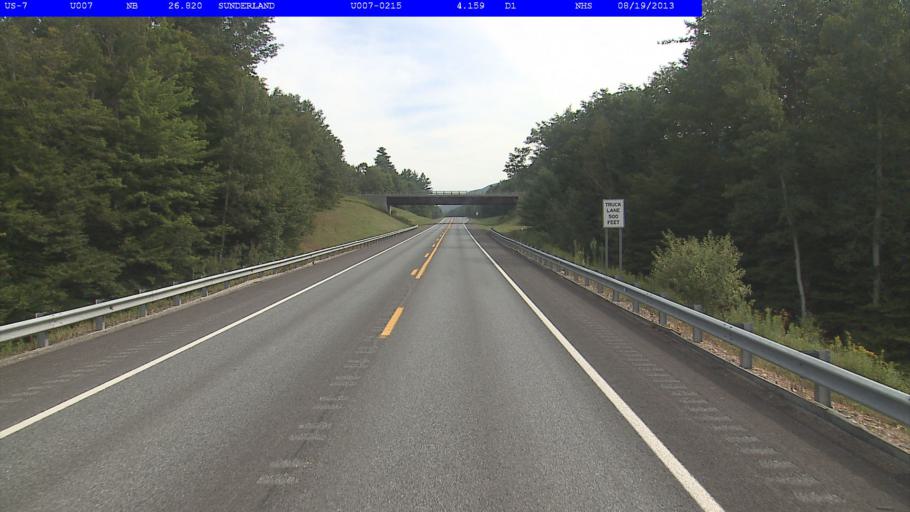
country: US
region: Vermont
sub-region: Bennington County
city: Arlington
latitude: 43.0818
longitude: -73.1122
